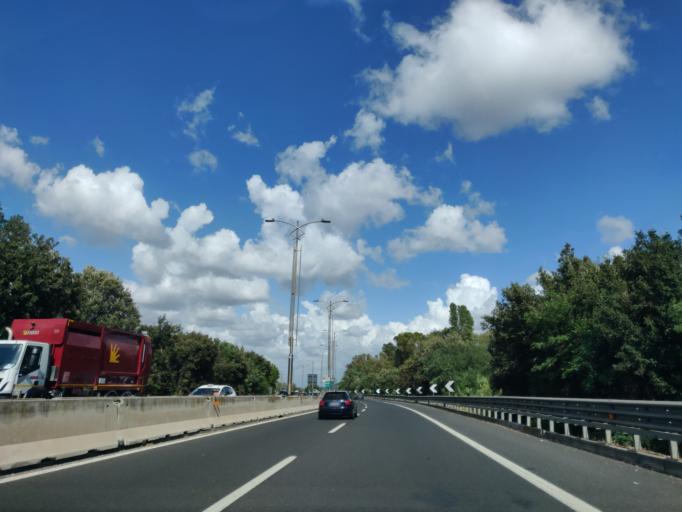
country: IT
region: Latium
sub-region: Citta metropolitana di Roma Capitale
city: Vitinia
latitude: 41.8202
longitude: 12.4122
